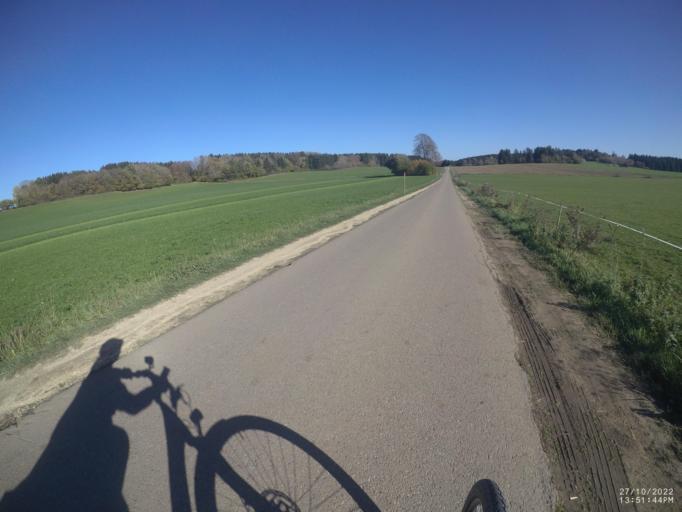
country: DE
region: Baden-Wuerttemberg
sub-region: Regierungsbezirk Stuttgart
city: Bad Ditzenbach
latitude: 48.5615
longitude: 9.7082
